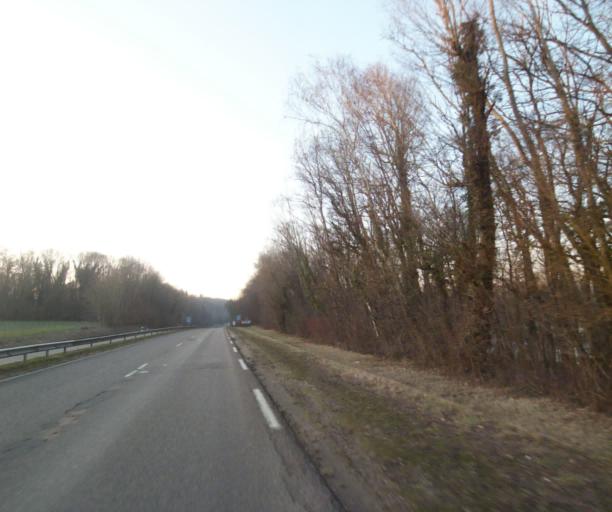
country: FR
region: Lorraine
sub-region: Departement de la Meuse
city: Ancerville
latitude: 48.6102
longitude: 5.0090
